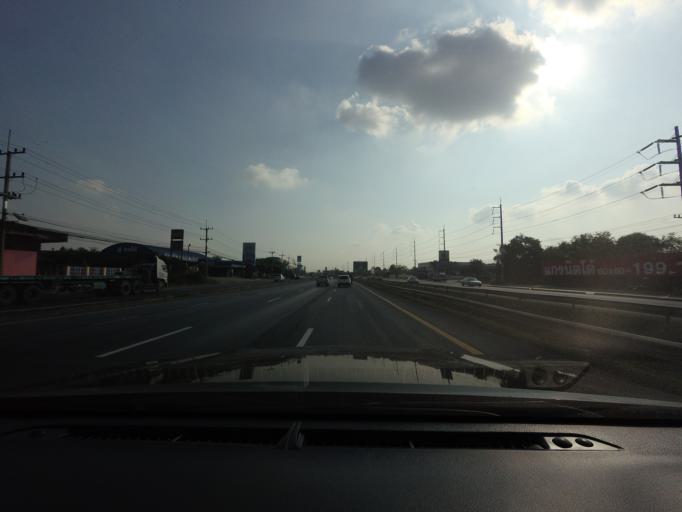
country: TH
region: Sara Buri
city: Saraburi
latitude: 14.4387
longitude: 100.8972
